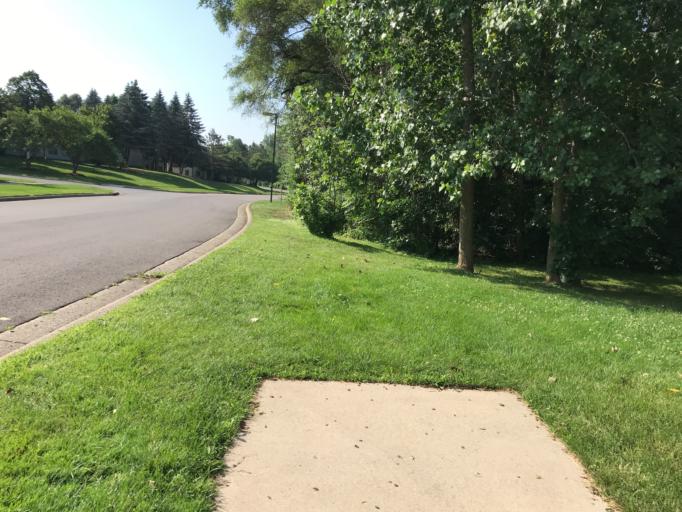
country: US
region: Michigan
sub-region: Washtenaw County
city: Ann Arbor
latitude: 42.2430
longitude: -83.7167
